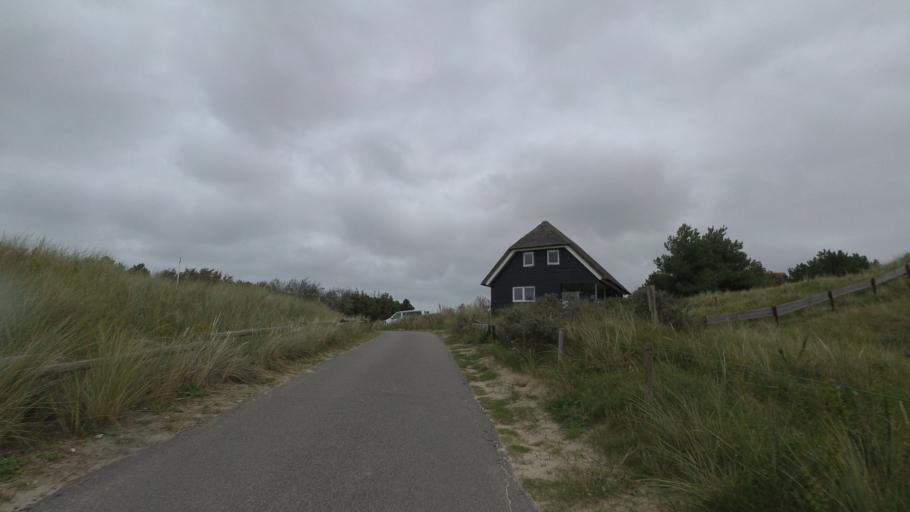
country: NL
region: Friesland
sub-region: Gemeente Ameland
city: Nes
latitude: 53.4562
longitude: 5.7905
